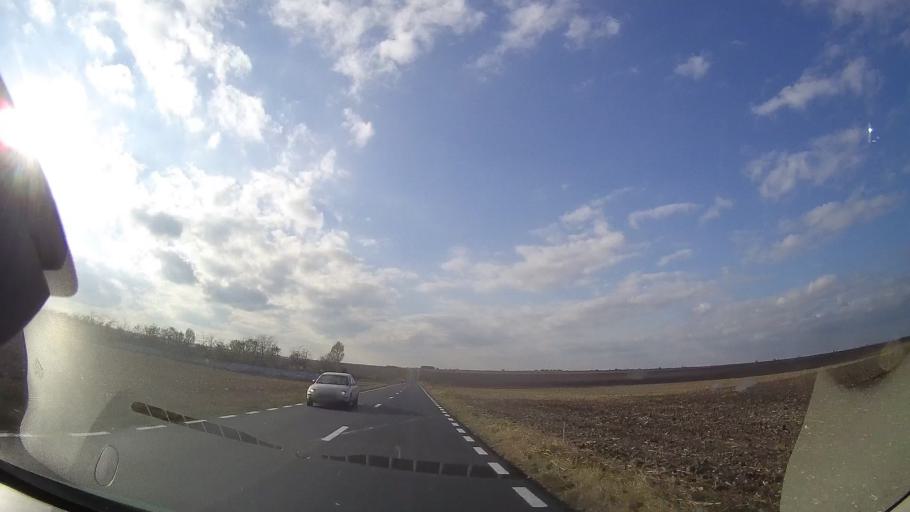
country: RO
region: Constanta
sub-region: Comuna Limanu
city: Limanu
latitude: 43.8245
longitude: 28.5052
